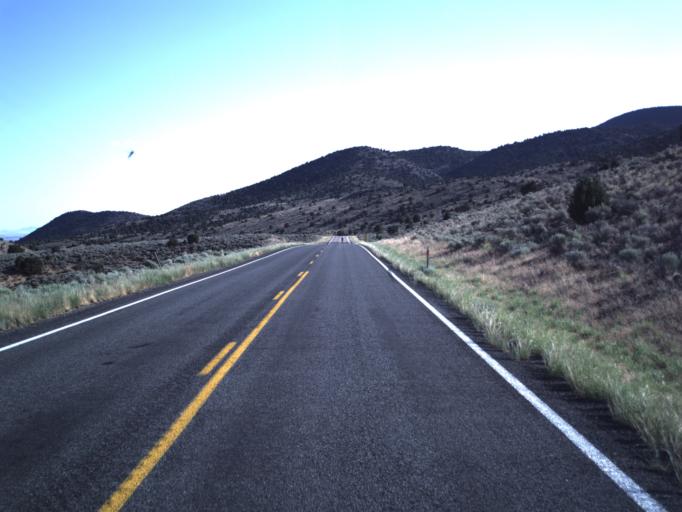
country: US
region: Utah
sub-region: Iron County
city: Parowan
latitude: 38.1011
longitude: -112.9490
